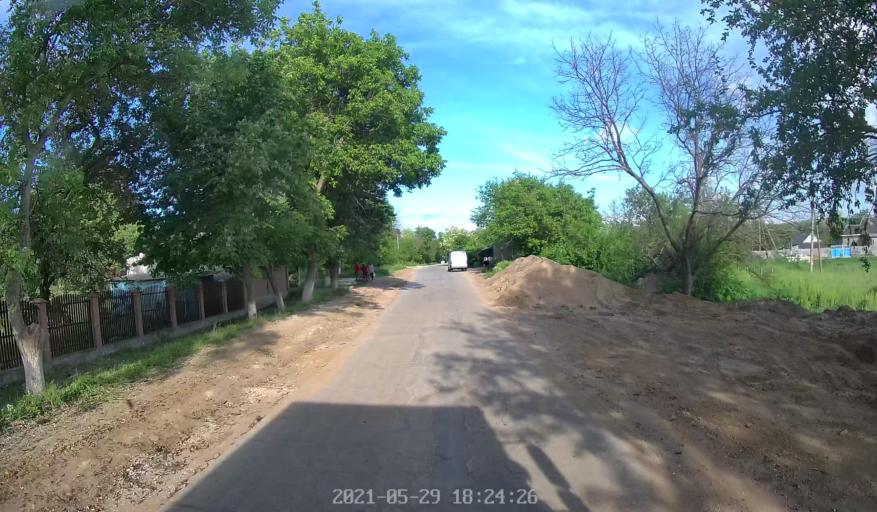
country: MD
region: Chisinau
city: Singera
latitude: 46.8297
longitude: 28.8631
